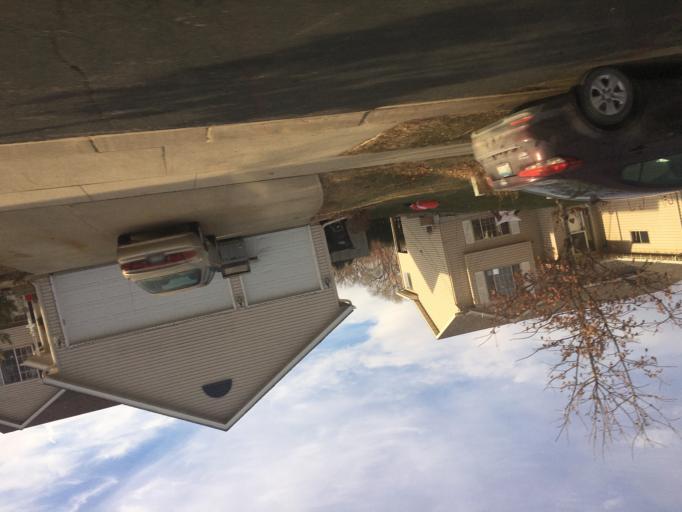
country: US
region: Minnesota
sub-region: Olmsted County
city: Oronoco
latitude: 44.0859
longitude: -92.5352
